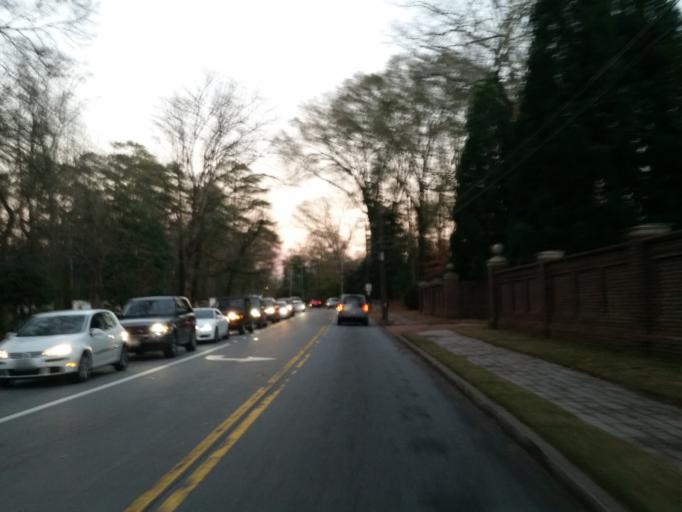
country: US
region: Georgia
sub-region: Cobb County
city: Vinings
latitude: 33.8455
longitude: -84.4043
